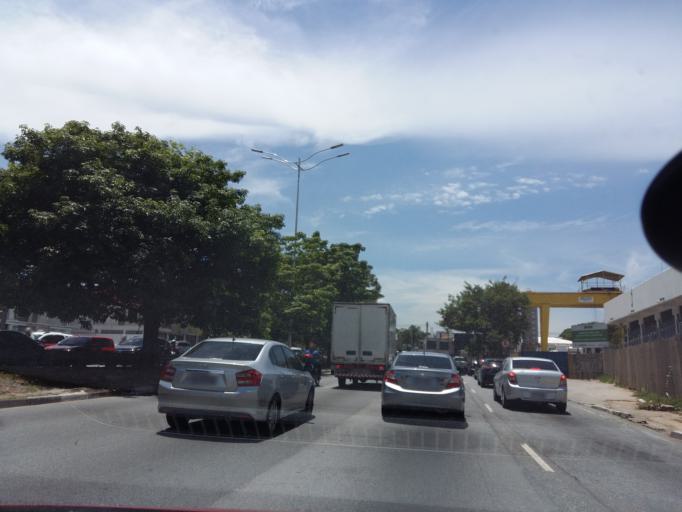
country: BR
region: Sao Paulo
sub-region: Sao Paulo
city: Sao Paulo
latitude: -23.6114
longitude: -46.6743
